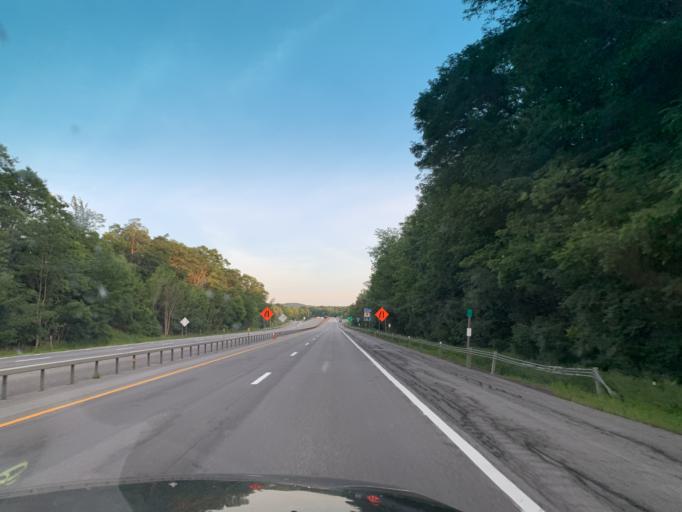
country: US
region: New York
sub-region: Oneida County
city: Chadwicks
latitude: 43.0116
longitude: -75.2549
